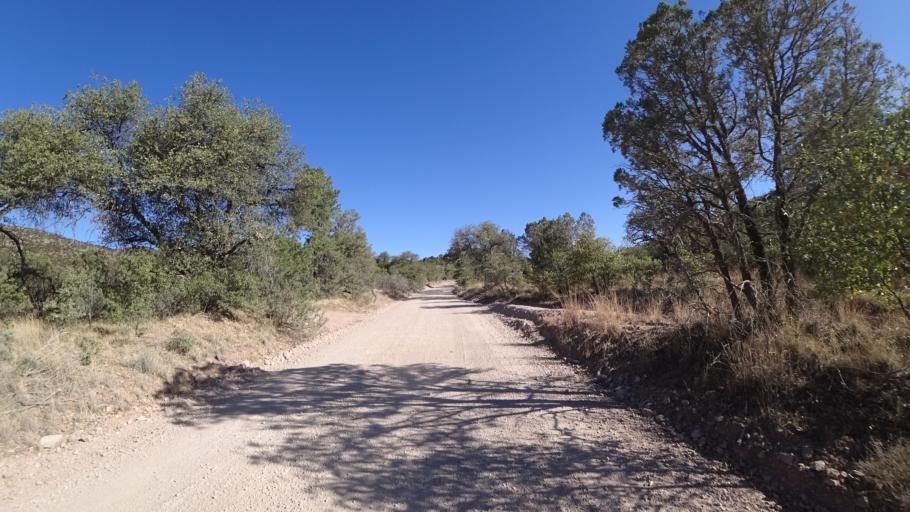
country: US
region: Arizona
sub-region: Cochise County
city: Huachuca City
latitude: 31.5048
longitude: -110.5583
